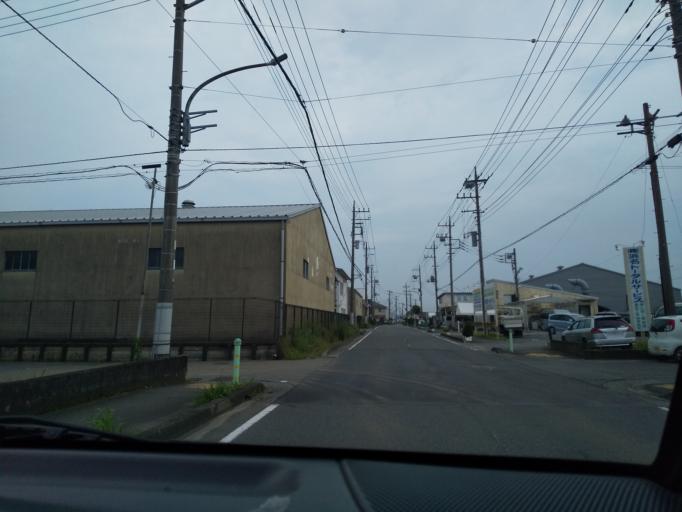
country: JP
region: Kanagawa
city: Atsugi
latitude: 35.4018
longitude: 139.3862
